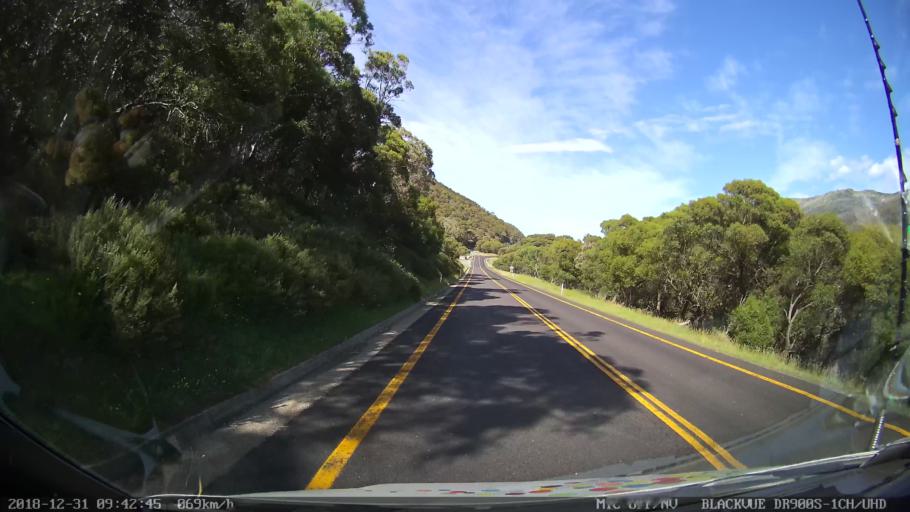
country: AU
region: New South Wales
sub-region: Snowy River
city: Jindabyne
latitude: -36.4983
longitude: 148.3195
